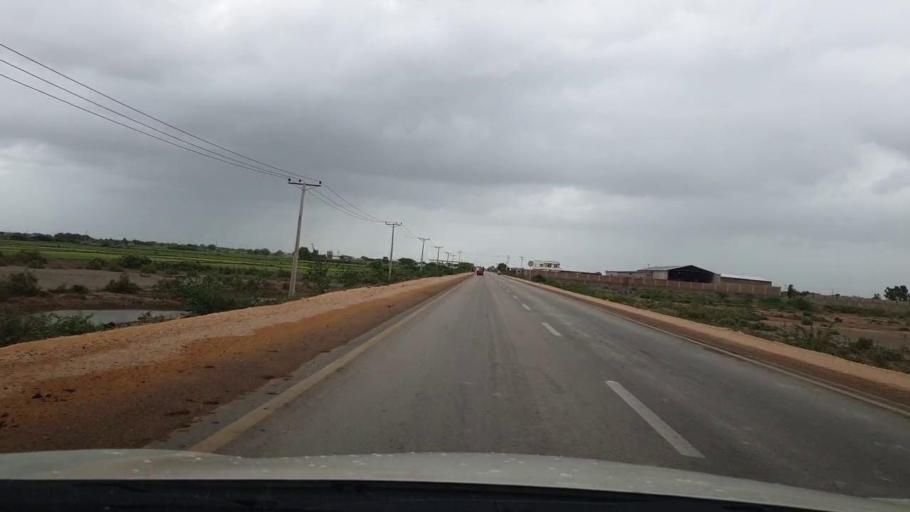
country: PK
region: Sindh
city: Badin
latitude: 24.6530
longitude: 68.7697
